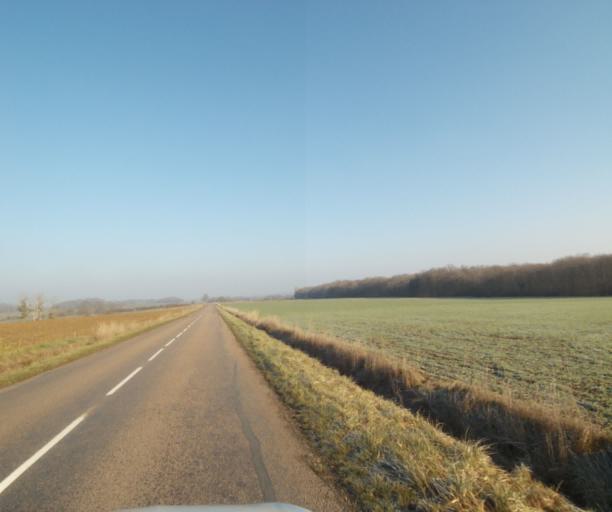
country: FR
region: Champagne-Ardenne
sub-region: Departement de la Haute-Marne
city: Montier-en-Der
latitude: 48.4351
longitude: 4.7542
